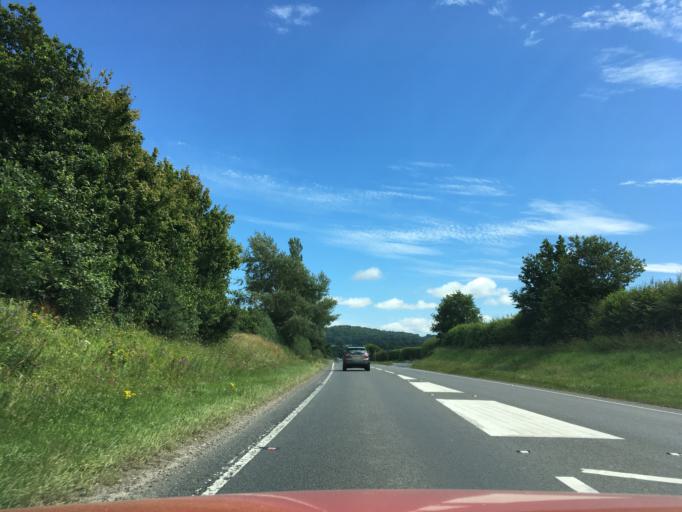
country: GB
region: England
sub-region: Somerset
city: Yeovil
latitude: 50.8805
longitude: -2.6036
